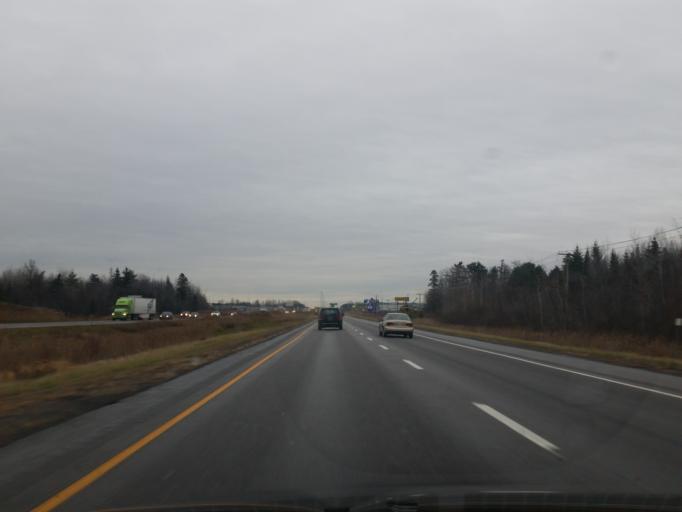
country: CA
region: Quebec
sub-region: Capitale-Nationale
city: Saint-Augustin-de-Desmaures
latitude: 46.7608
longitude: -71.4467
